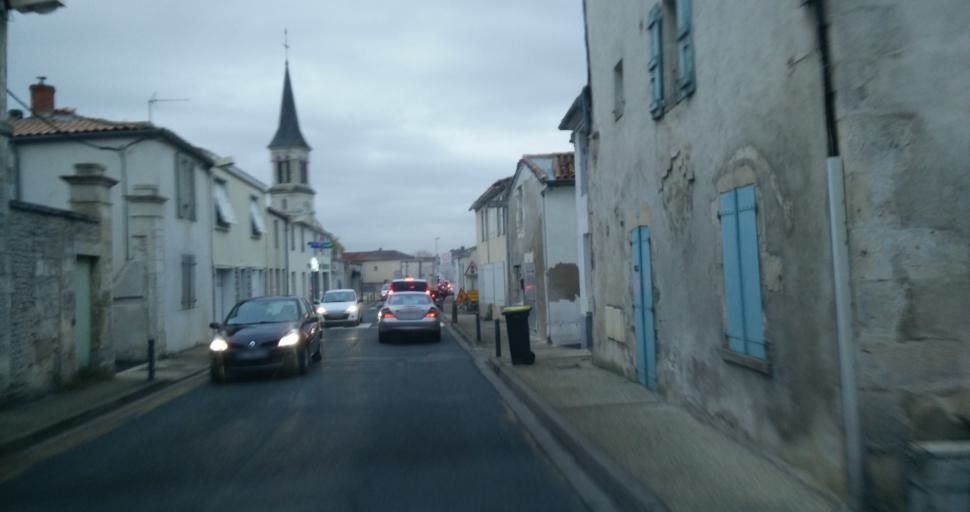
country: FR
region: Poitou-Charentes
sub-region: Departement de la Charente-Maritime
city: Puilboreau
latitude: 46.1864
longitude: -1.1184
